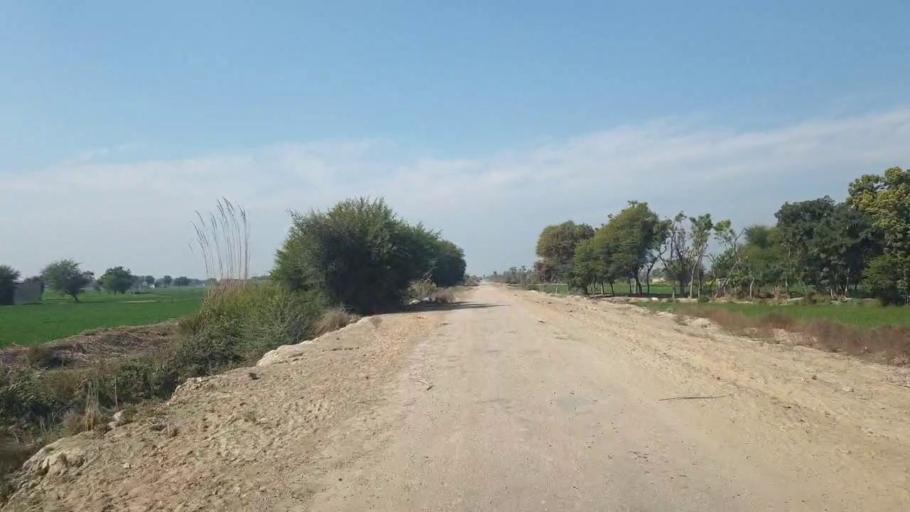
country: PK
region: Sindh
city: Shahdadpur
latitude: 25.9939
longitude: 68.5284
